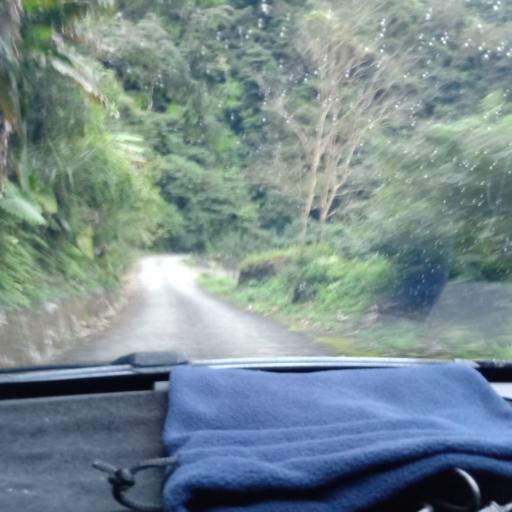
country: TW
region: Taiwan
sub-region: Yilan
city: Yilan
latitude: 24.8096
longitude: 121.6983
